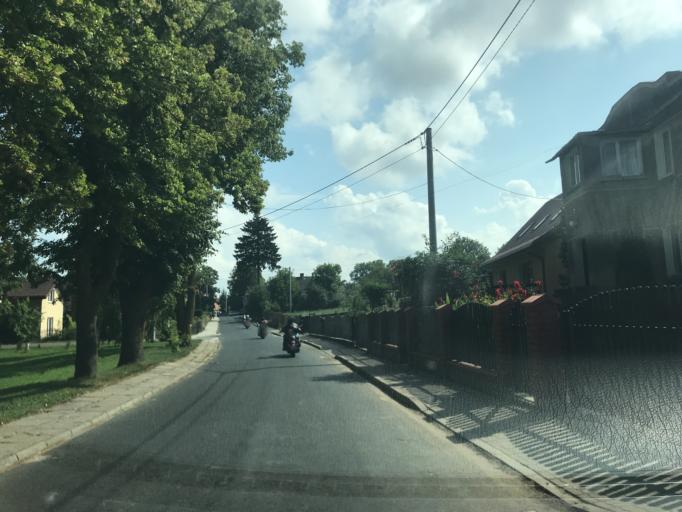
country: PL
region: Warmian-Masurian Voivodeship
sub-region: Powiat nowomiejski
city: Biskupiec
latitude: 53.4643
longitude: 19.4692
